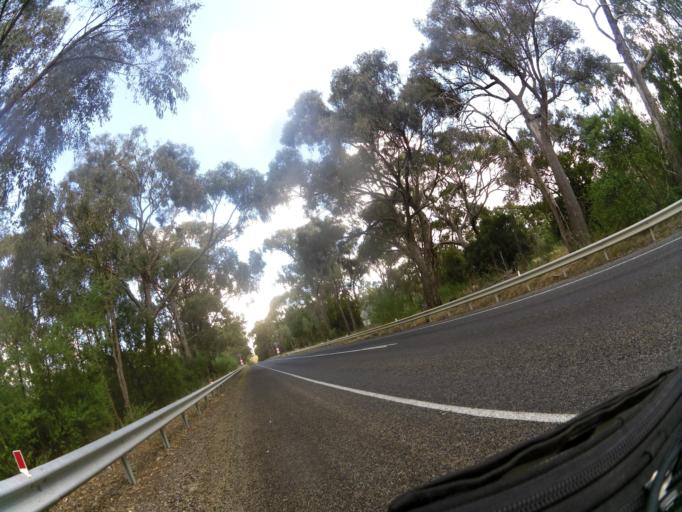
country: AU
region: Victoria
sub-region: Mansfield
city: Mansfield
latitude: -36.8327
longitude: 146.0081
